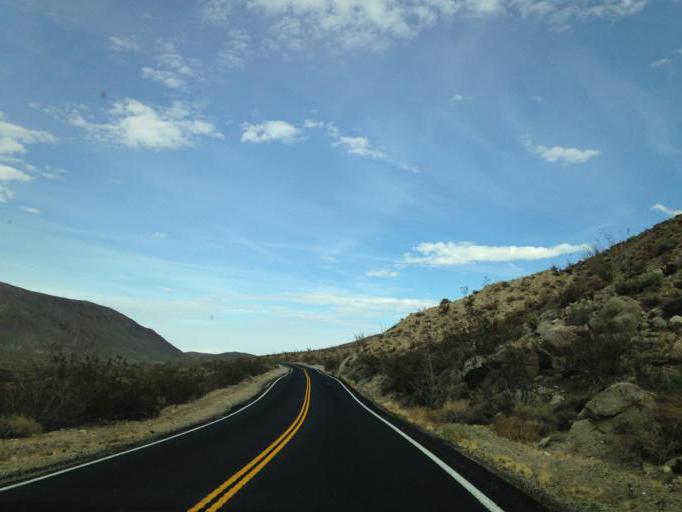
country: US
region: California
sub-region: San Diego County
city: Borrego Springs
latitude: 33.1317
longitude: -116.3966
